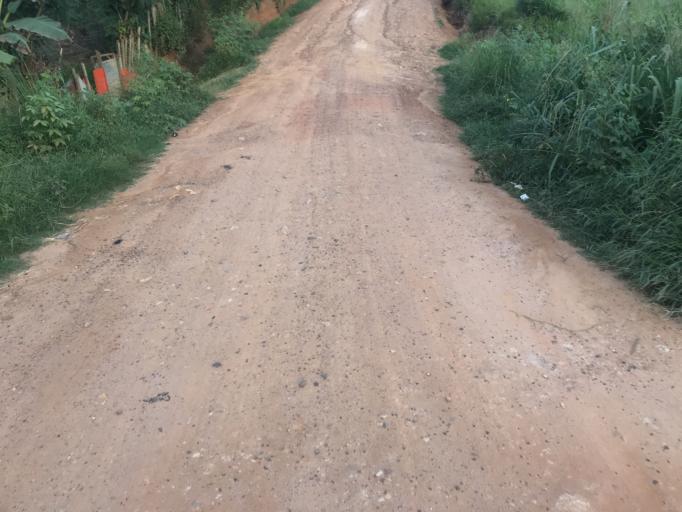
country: GH
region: Ashanti
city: Obuasi
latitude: 6.2051
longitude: -1.6006
